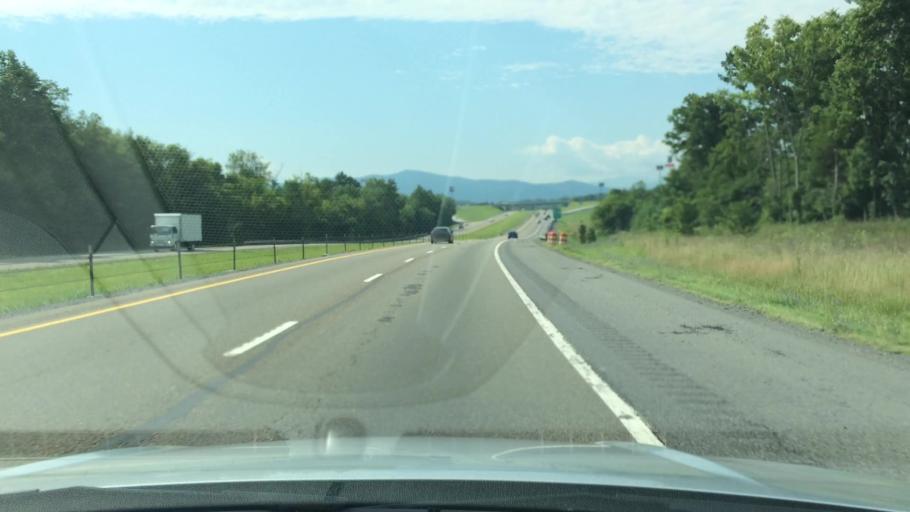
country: US
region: Tennessee
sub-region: Cocke County
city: Newport
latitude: 35.9550
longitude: -83.2066
